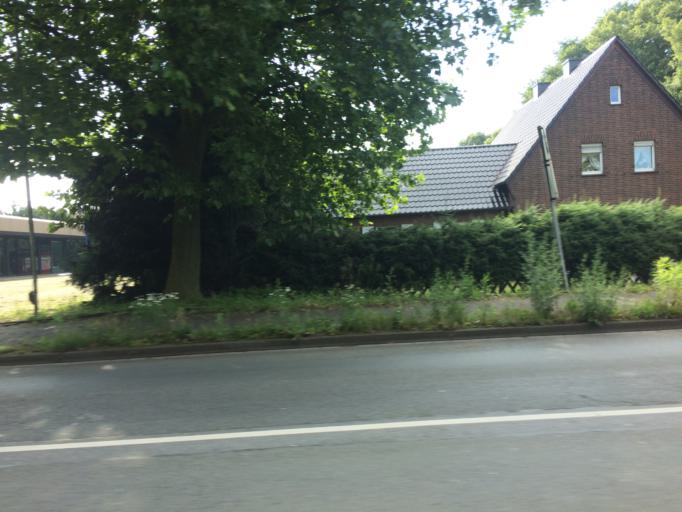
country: DE
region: North Rhine-Westphalia
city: Dorsten
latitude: 51.7140
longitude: 7.0118
